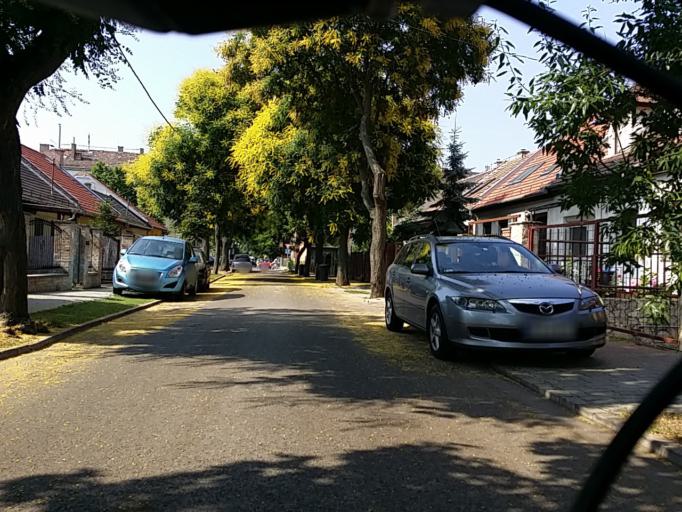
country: HU
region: Budapest
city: Budapest IV. keruelet
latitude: 47.5485
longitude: 19.0827
